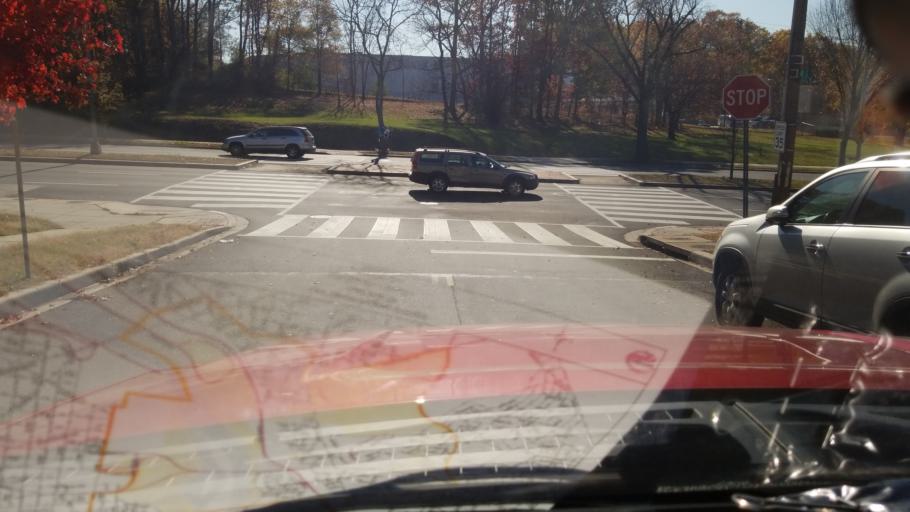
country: US
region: Maryland
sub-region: Prince George's County
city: Capitol Heights
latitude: 38.8902
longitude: -76.9473
